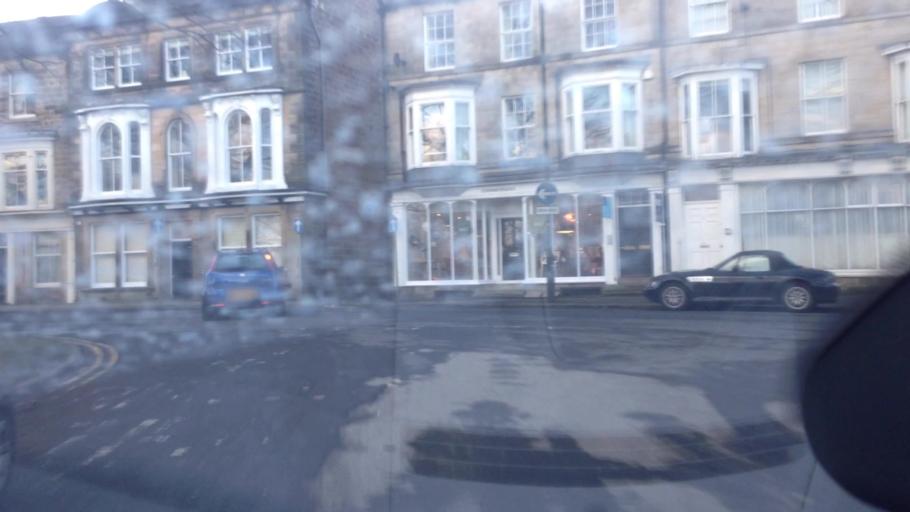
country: GB
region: England
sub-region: North Yorkshire
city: Harrogate
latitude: 53.9969
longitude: -1.5283
